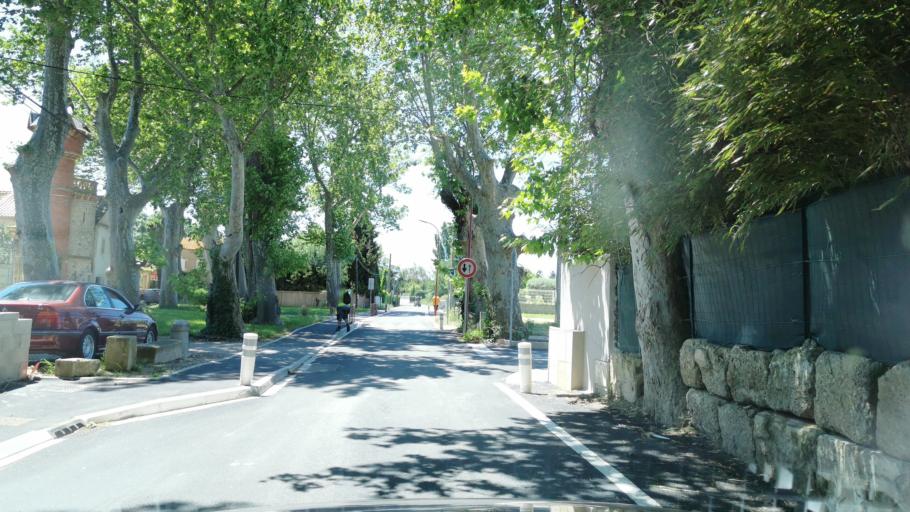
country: FR
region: Languedoc-Roussillon
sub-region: Departement de l'Aude
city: Saint-Marcel-sur-Aude
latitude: 43.2615
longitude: 2.9568
